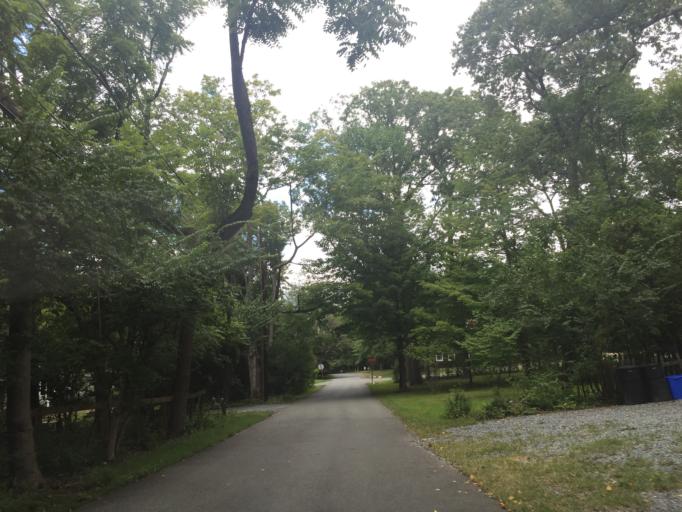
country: US
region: Maryland
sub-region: Montgomery County
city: Gaithersburg
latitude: 39.1398
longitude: -77.1767
